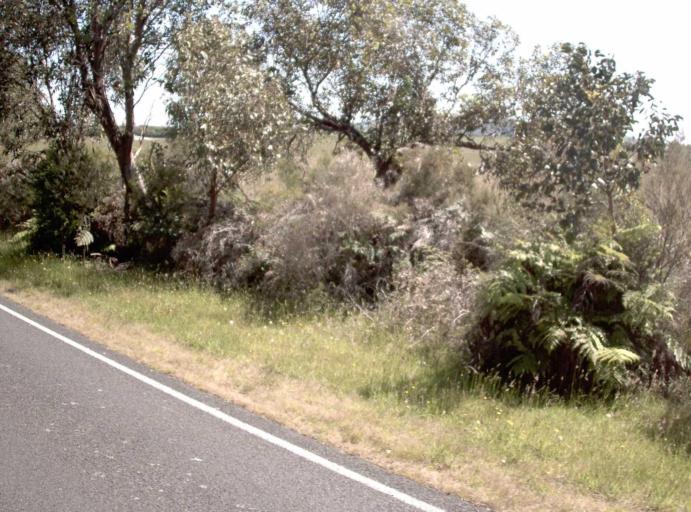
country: AU
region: Victoria
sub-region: Latrobe
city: Morwell
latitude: -38.6728
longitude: 146.1939
